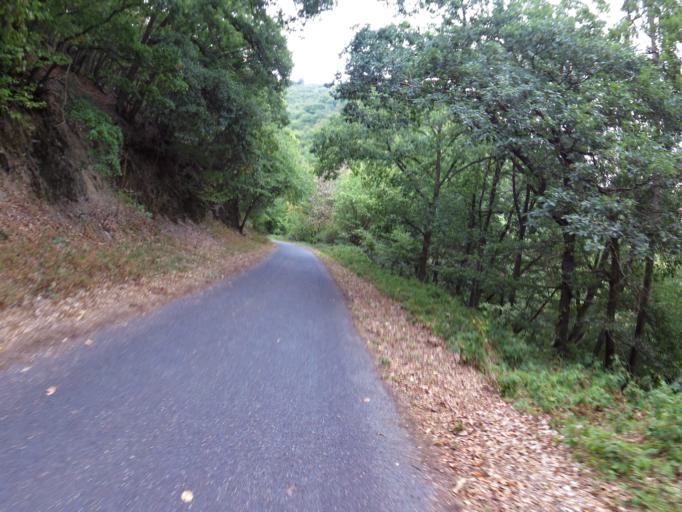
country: DE
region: North Rhine-Westphalia
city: Heimbach
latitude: 50.6205
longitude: 6.3960
